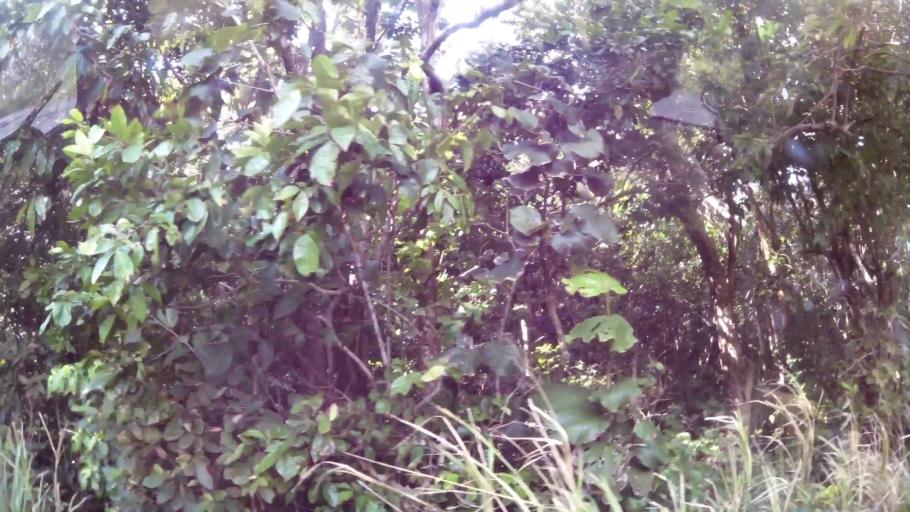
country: DM
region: Saint Andrew
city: Calibishie
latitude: 15.5968
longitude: -61.3643
